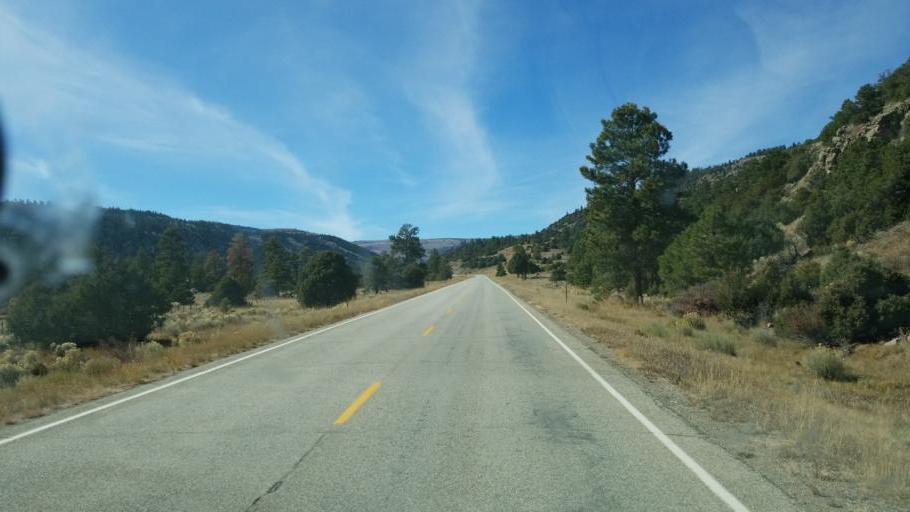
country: US
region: Colorado
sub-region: Conejos County
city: Conejos
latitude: 37.0680
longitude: -106.2351
